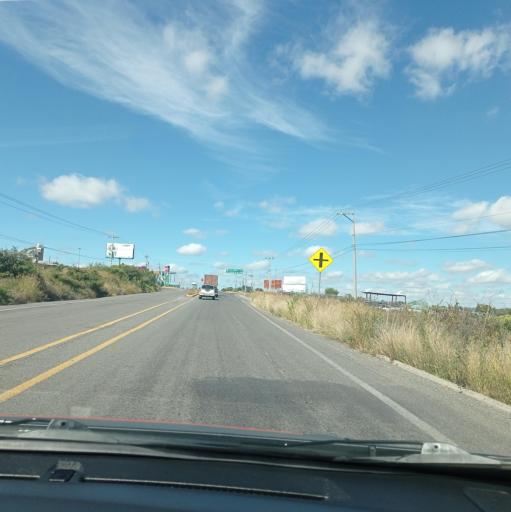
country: MX
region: Jalisco
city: San Miguel el Alto
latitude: 21.0140
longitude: -102.3204
